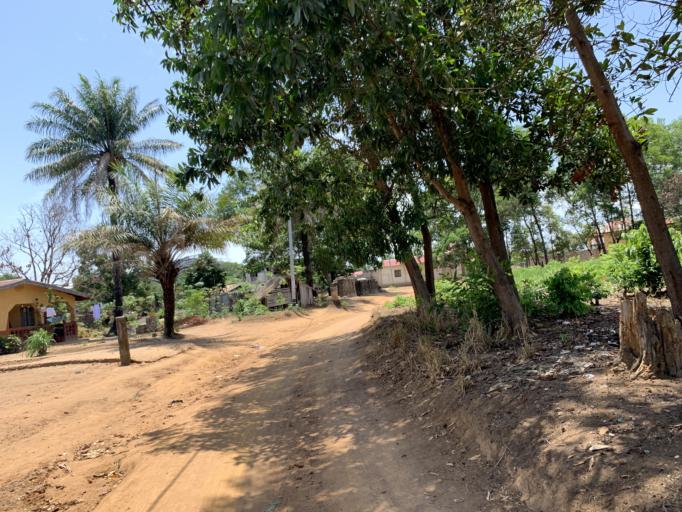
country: SL
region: Western Area
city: Waterloo
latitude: 8.3140
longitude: -13.0726
